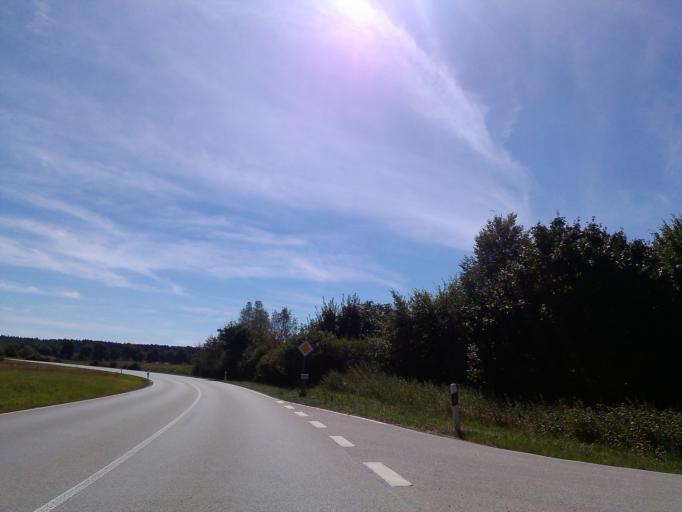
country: DE
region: Bavaria
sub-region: Upper Bavaria
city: Starnberg
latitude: 48.0283
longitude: 11.3218
